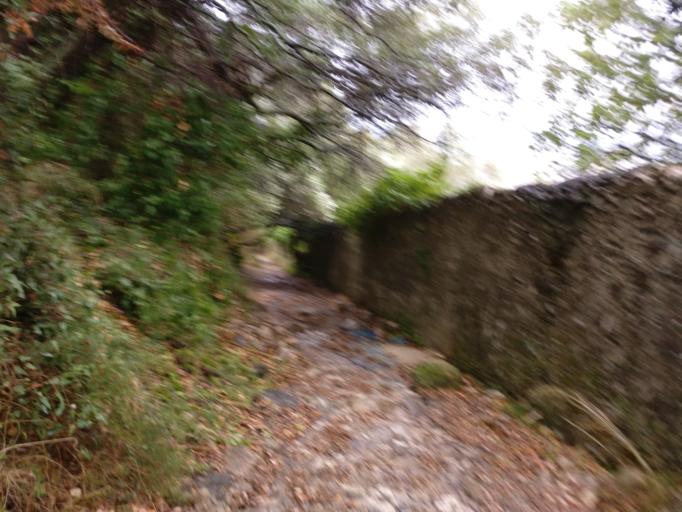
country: FR
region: Provence-Alpes-Cote d'Azur
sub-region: Departement des Alpes-Maritimes
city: Villefranche-sur-Mer
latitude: 43.7162
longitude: 7.2994
